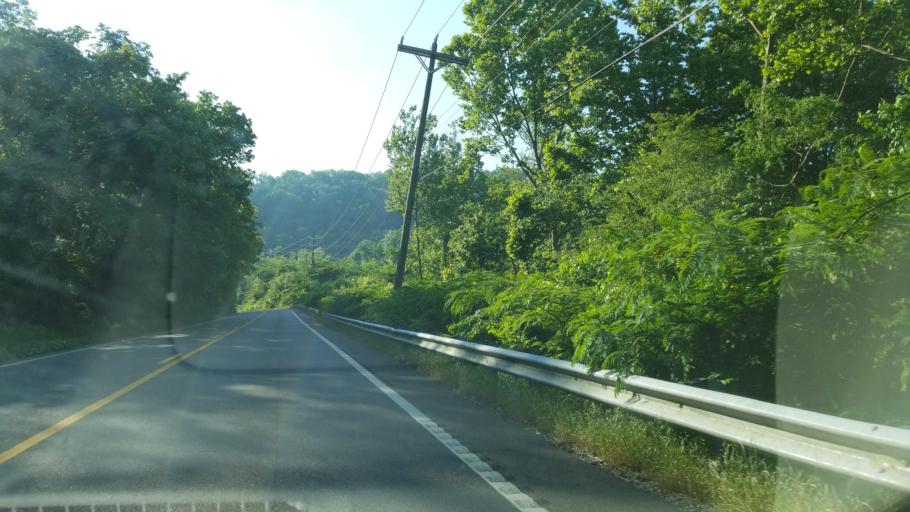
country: US
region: Tennessee
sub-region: Hamilton County
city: Collegedale
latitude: 35.0773
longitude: -85.0454
